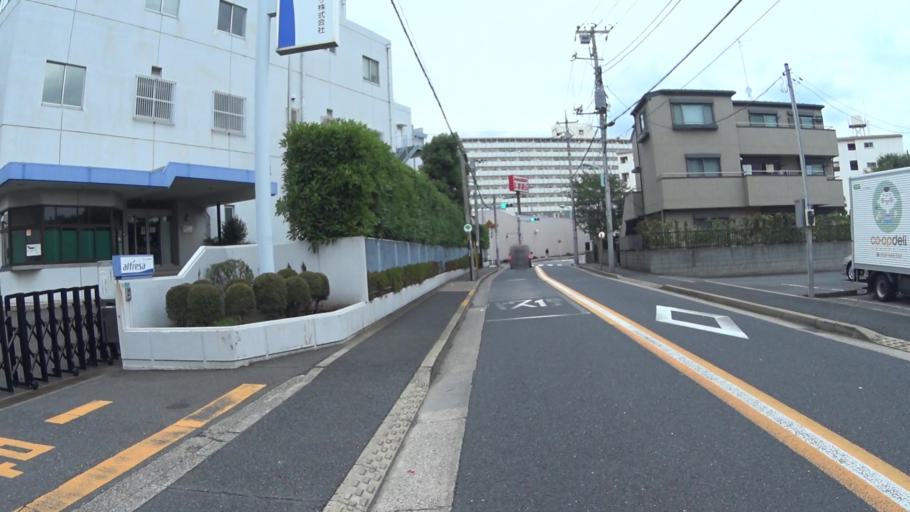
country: JP
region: Tokyo
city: Urayasu
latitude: 35.7160
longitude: 139.8358
